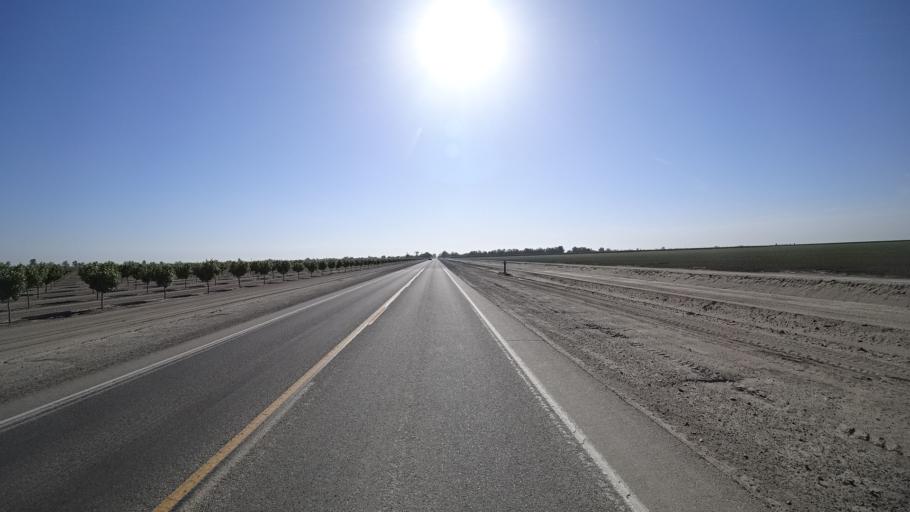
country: US
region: California
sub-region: Kings County
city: Corcoran
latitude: 36.0980
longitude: -119.6067
